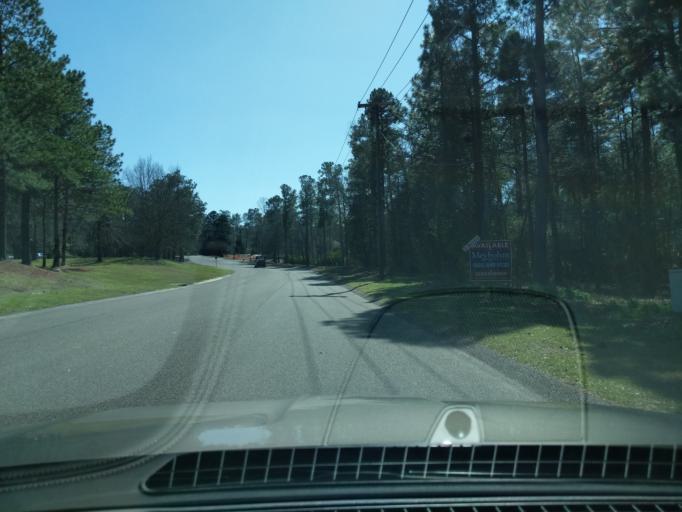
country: US
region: South Carolina
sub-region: Aiken County
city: Aiken
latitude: 33.5315
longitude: -81.7524
